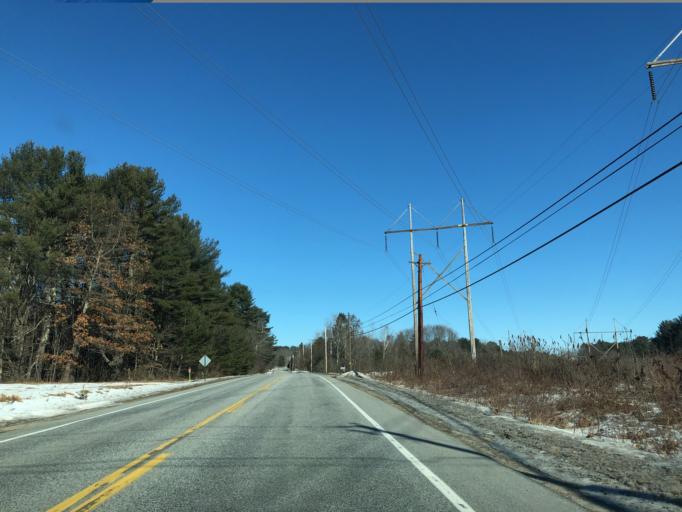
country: US
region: Maine
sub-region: Cumberland County
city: South Windham
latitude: 43.7518
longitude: -70.4247
